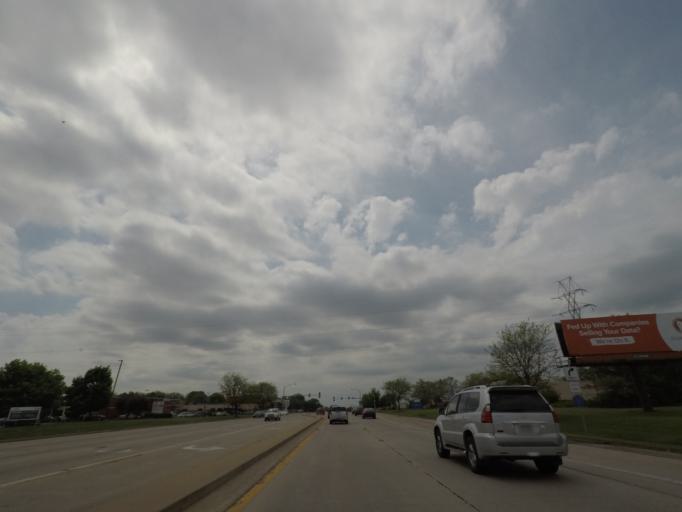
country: US
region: Illinois
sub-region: Winnebago County
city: Cherry Valley
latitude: 42.2687
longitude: -88.9801
